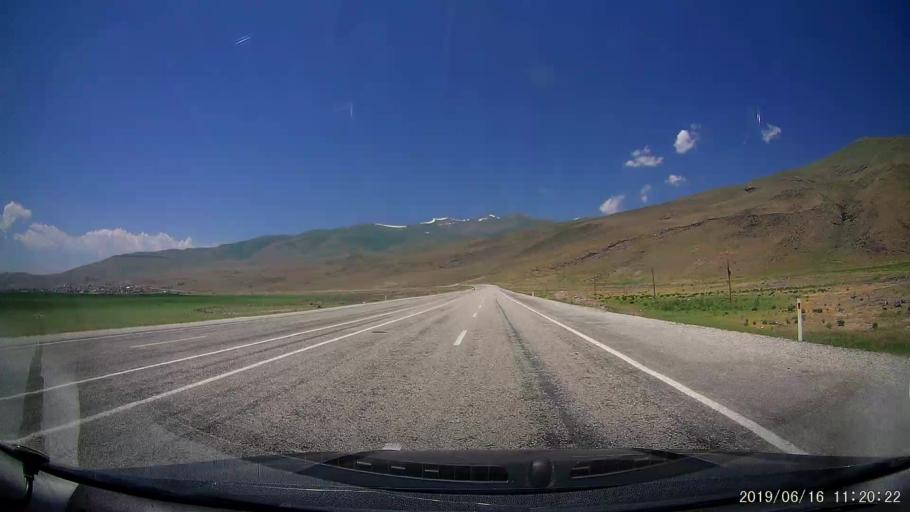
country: TR
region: Agri
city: Dogubayazit
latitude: 39.6986
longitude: 44.0919
